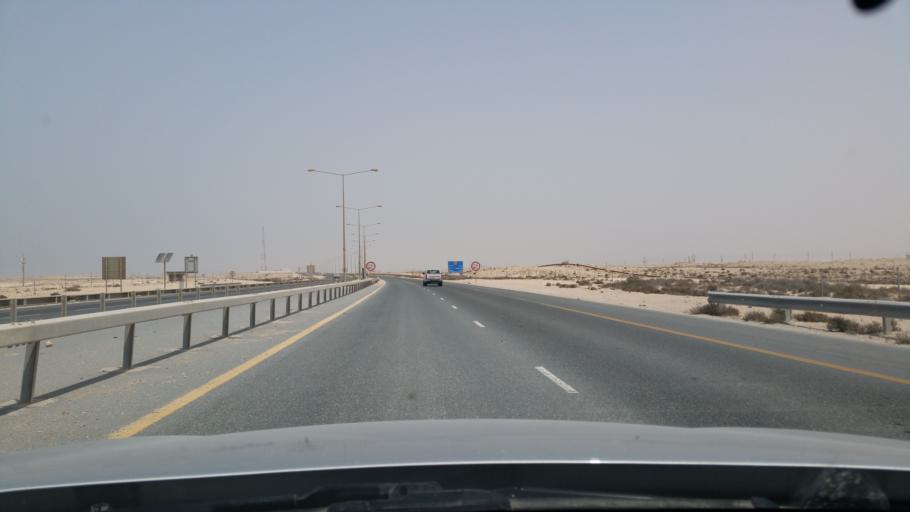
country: QA
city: Umm Bab
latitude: 25.2978
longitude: 50.7923
